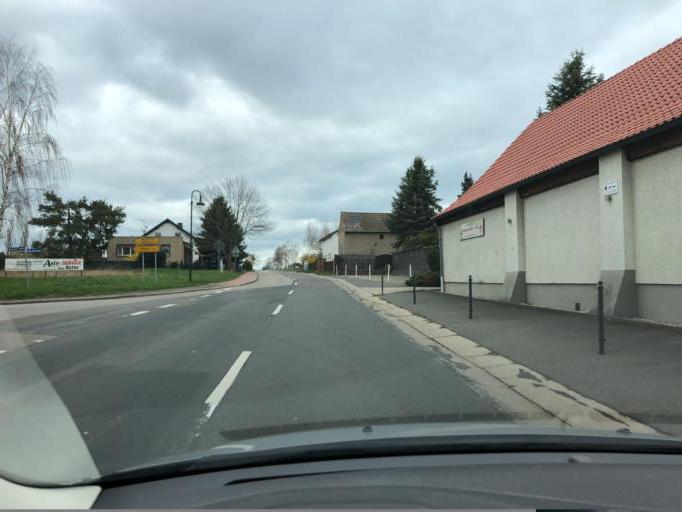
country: DE
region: Saxony-Anhalt
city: Muschwitz
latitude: 51.2179
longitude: 12.1403
